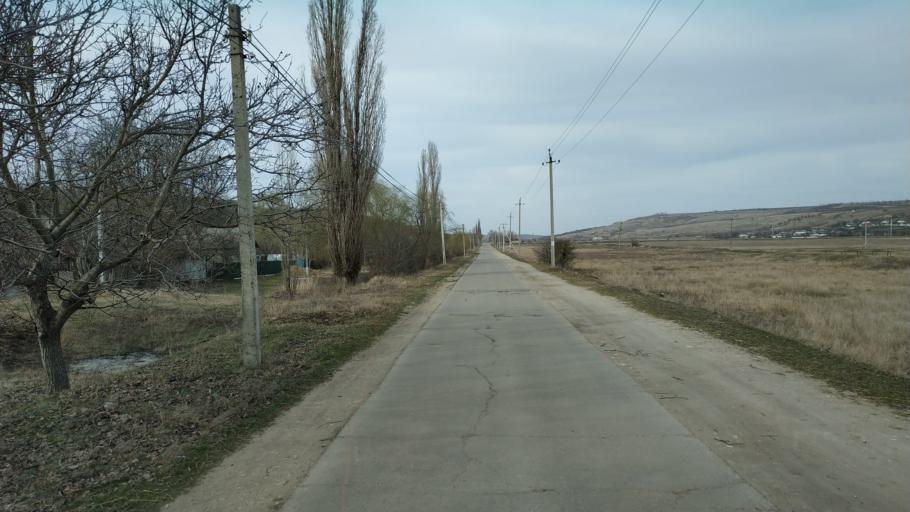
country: RO
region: Vaslui
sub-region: Comuna Dranceni
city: Dranceni
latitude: 46.8656
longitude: 28.2005
